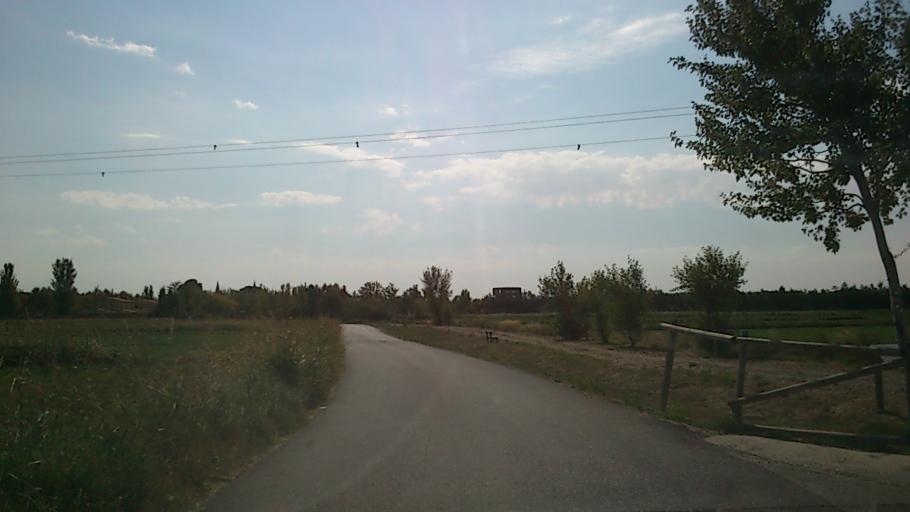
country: ES
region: Aragon
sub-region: Provincia de Zaragoza
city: Puebla de Alfinden
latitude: 41.6100
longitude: -0.7598
